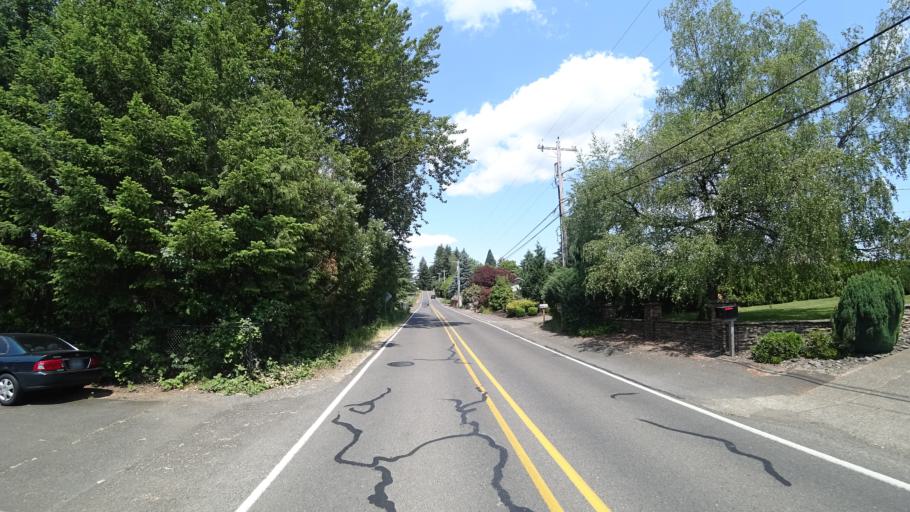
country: US
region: Oregon
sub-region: Clackamas County
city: Happy Valley
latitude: 45.4476
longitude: -122.5432
